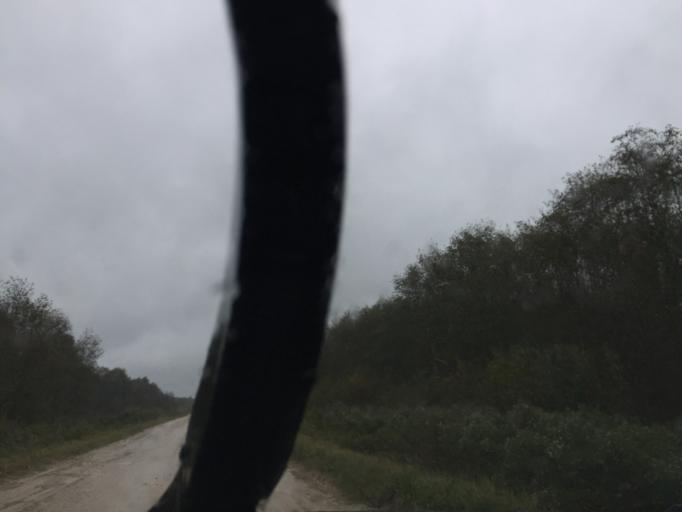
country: LV
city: Tireli
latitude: 56.7484
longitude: 23.5302
